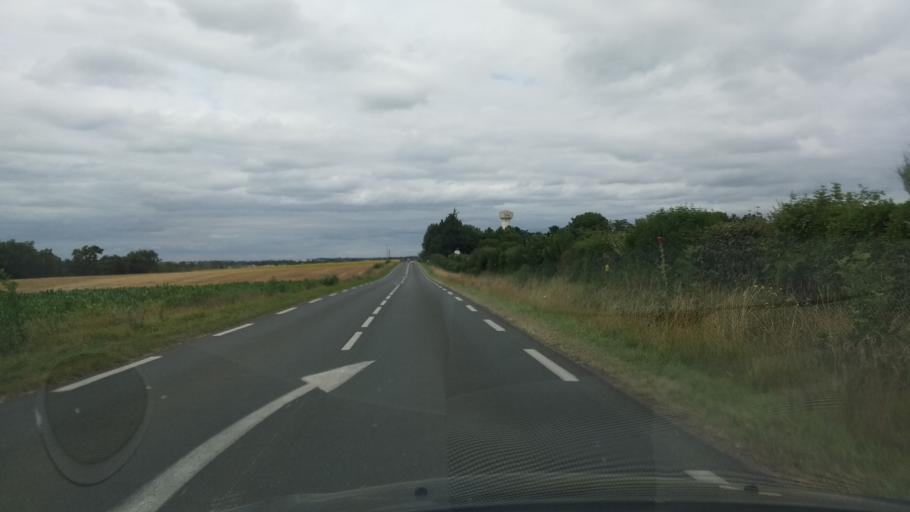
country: FR
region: Poitou-Charentes
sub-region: Departement de la Vienne
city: La Villedieu-du-Clain
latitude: 46.4638
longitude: 0.3674
